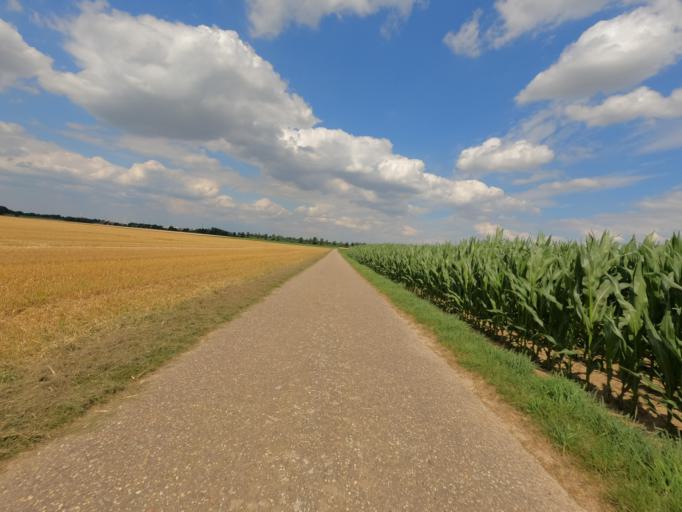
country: DE
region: North Rhine-Westphalia
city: Geilenkirchen
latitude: 50.9601
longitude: 6.0840
